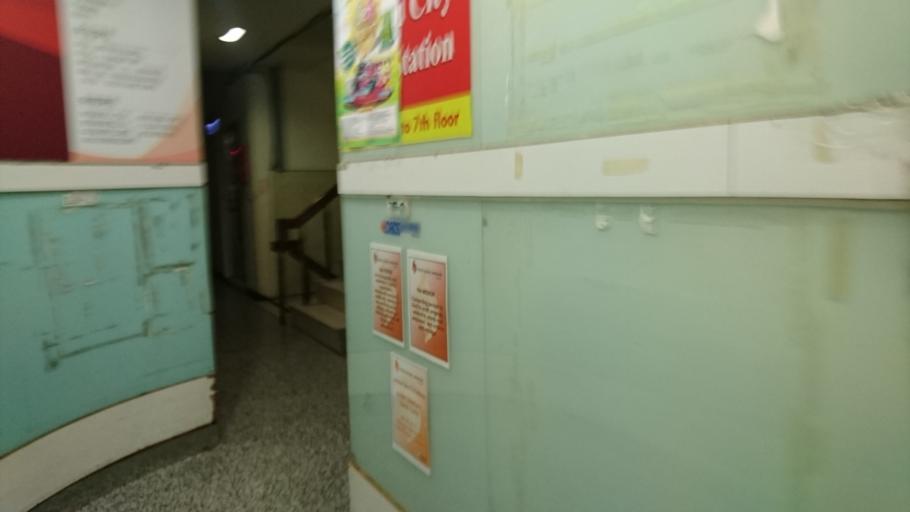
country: TW
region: Taiwan
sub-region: Hsinchu
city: Hsinchu
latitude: 24.8031
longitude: 120.9712
